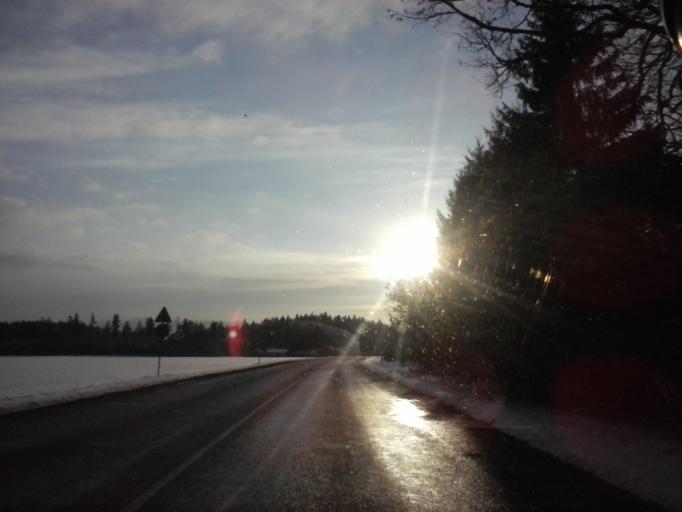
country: EE
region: Tartu
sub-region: UElenurme vald
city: Ulenurme
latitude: 58.3463
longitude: 26.9123
